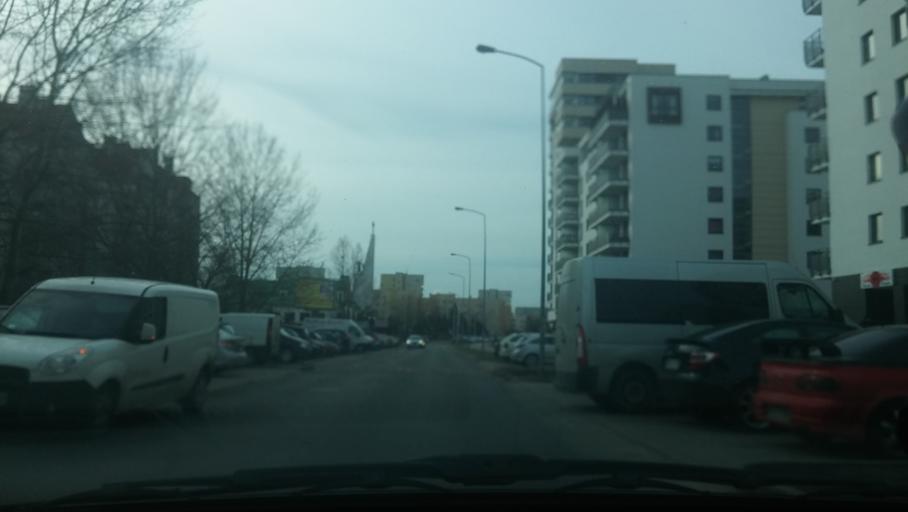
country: PL
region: Masovian Voivodeship
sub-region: Warszawa
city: Praga Poludnie
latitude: 52.2291
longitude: 21.1062
